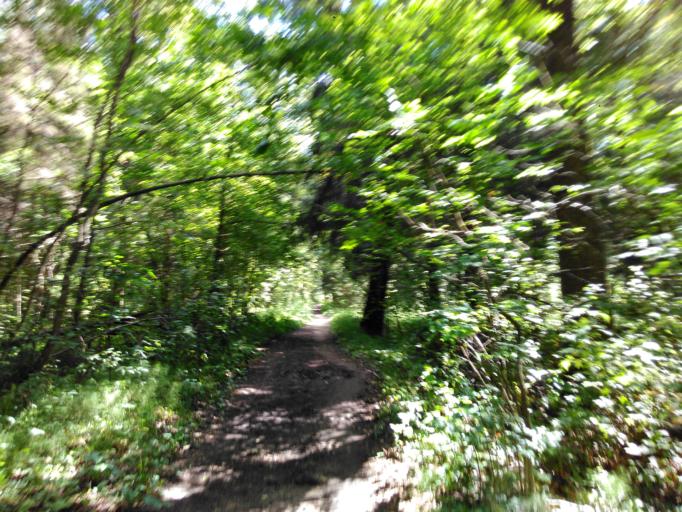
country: RU
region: Tverskaya
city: Konakovo
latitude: 56.6841
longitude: 36.7081
